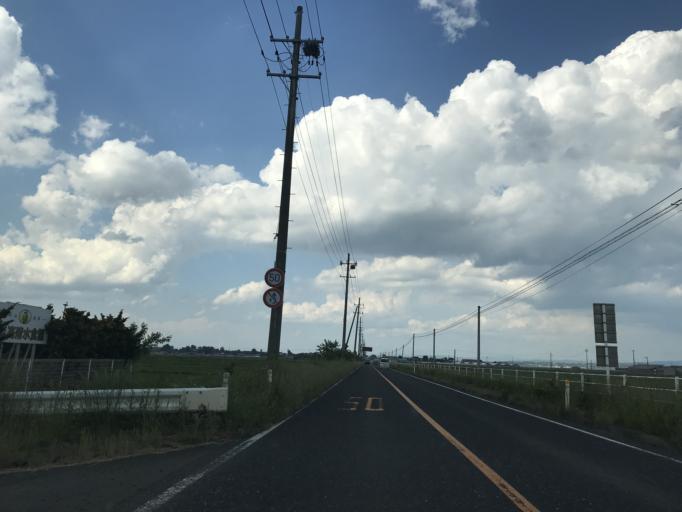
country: JP
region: Miyagi
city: Wakuya
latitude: 38.6003
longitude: 141.1693
